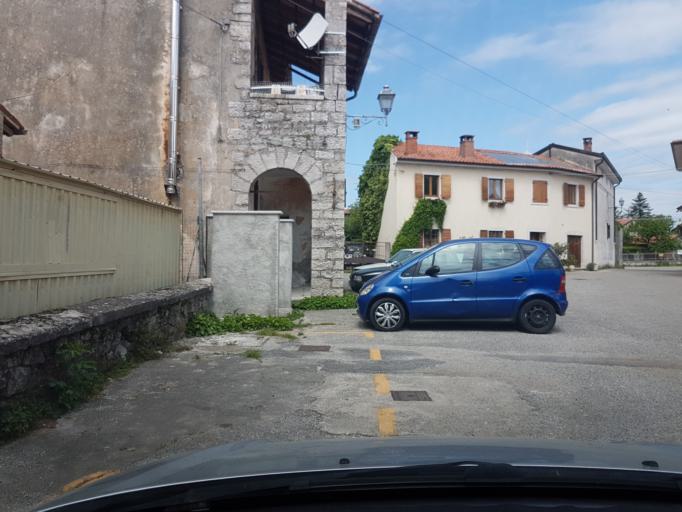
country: IT
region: Friuli Venezia Giulia
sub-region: Provincia di Trieste
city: Sistiana-Visogliano
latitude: 45.7854
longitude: 13.6598
